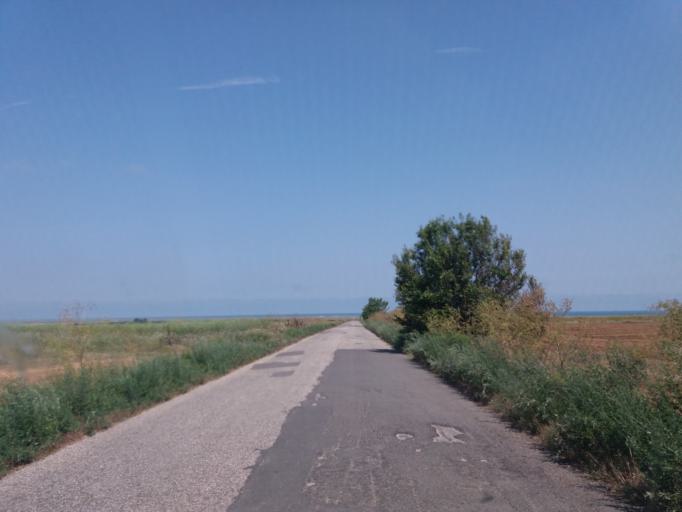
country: RO
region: Constanta
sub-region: Comuna Corbu
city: Corbu
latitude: 44.4261
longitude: 28.7071
